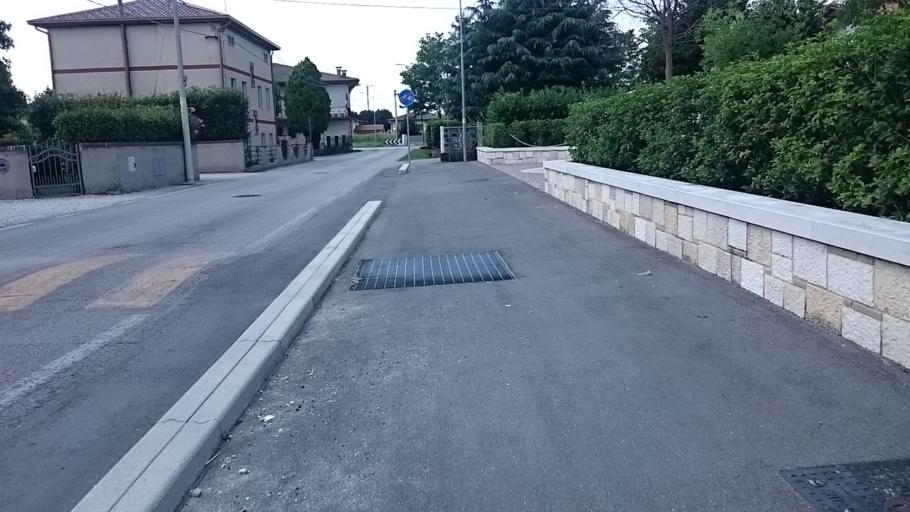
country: IT
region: Veneto
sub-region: Provincia di Vicenza
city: Rosa
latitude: 45.7056
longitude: 11.7381
